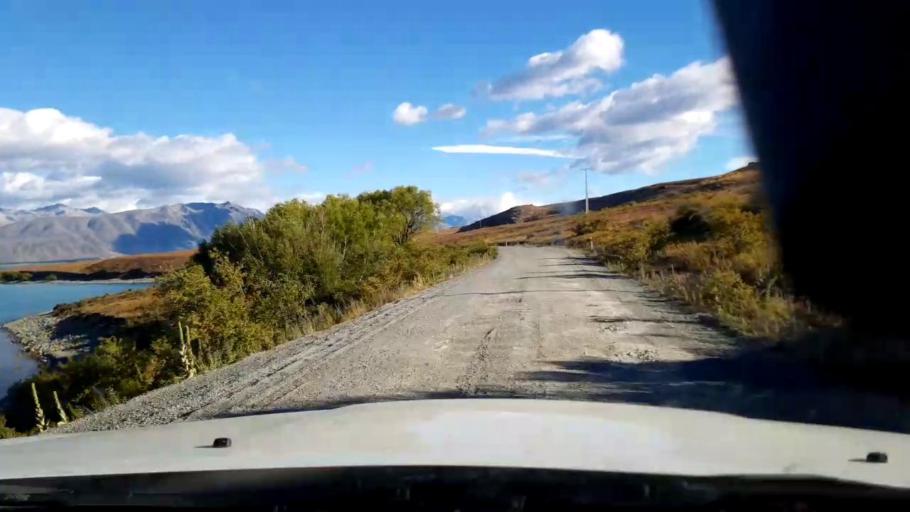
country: NZ
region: Canterbury
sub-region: Timaru District
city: Pleasant Point
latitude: -43.9272
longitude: 170.5604
